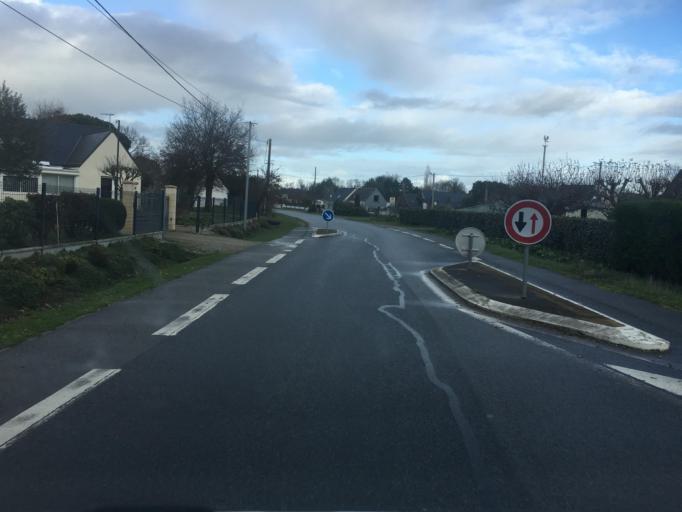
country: FR
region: Brittany
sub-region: Departement du Morbihan
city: Surzur
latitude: 47.5214
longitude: -2.6548
